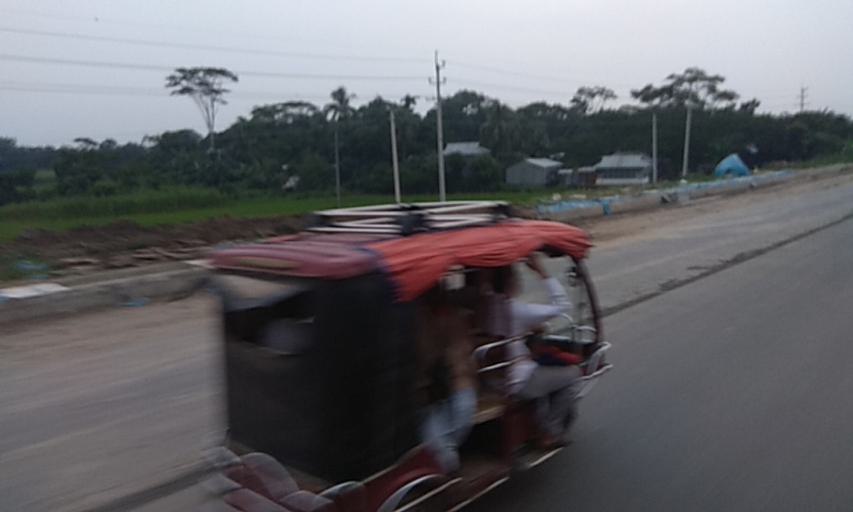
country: BD
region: Dhaka
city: Char Bhadrasan
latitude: 23.3751
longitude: 90.0235
